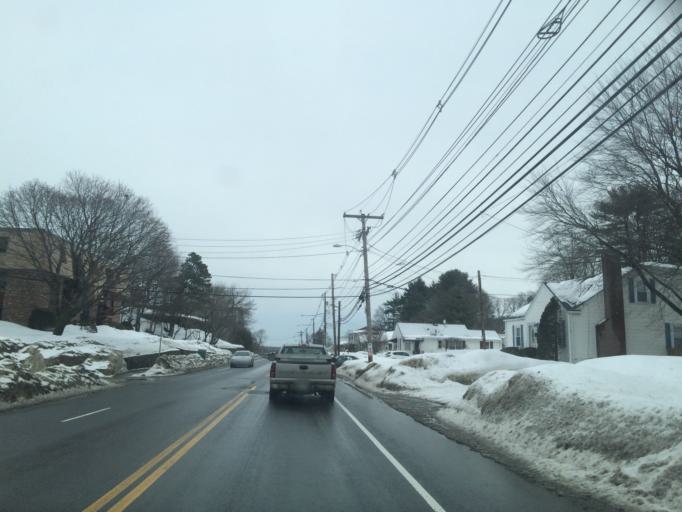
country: US
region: Massachusetts
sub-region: Middlesex County
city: Waltham
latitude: 42.3765
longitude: -71.2616
